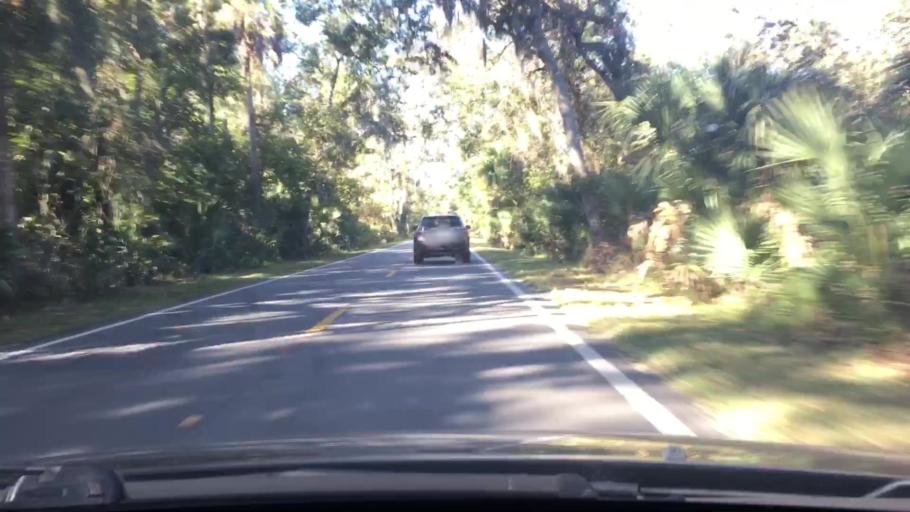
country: US
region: Florida
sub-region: Volusia County
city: Ormond-by-the-Sea
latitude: 29.3822
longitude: -81.1305
